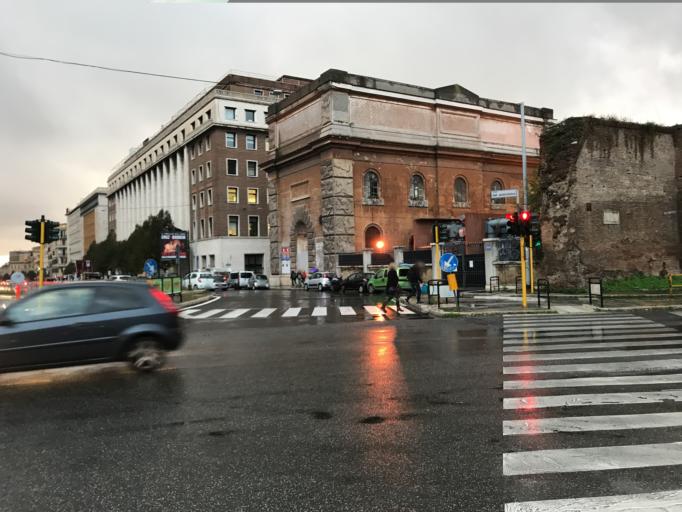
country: IT
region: Latium
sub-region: Citta metropolitana di Roma Capitale
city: Rome
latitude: 41.9082
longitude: 12.5045
